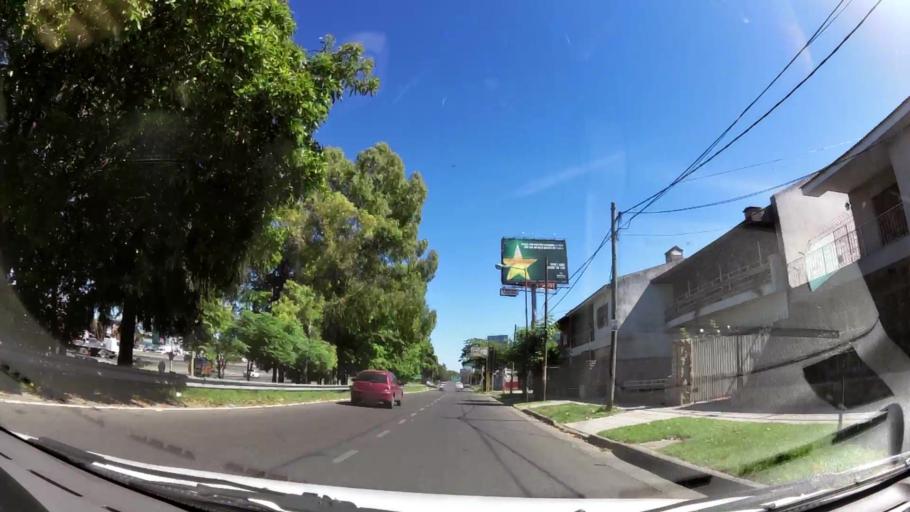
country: AR
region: Buenos Aires
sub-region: Partido de Vicente Lopez
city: Olivos
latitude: -34.5297
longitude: -58.5056
